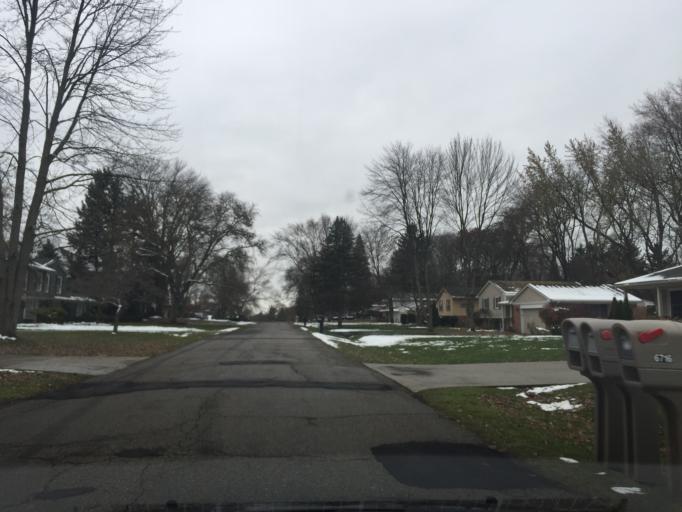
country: US
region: Michigan
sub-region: Oakland County
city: Franklin
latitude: 42.5416
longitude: -83.2918
